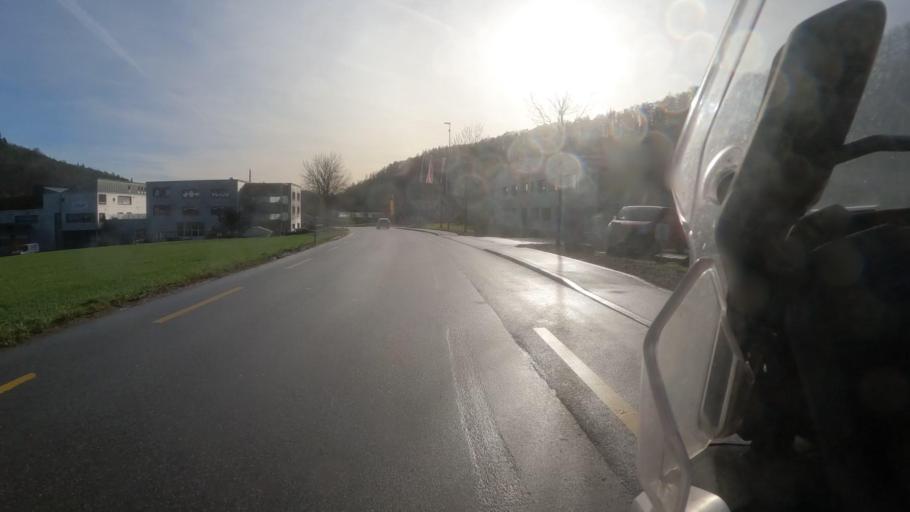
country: CH
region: Schaffhausen
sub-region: Bezirk Schaffhausen
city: Schaffhausen
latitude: 47.7318
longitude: 8.6216
